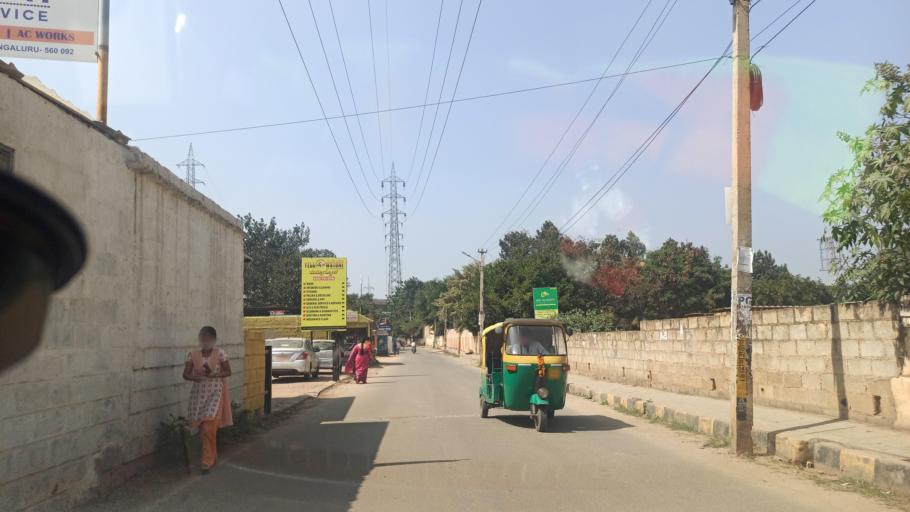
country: IN
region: Karnataka
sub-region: Bangalore Urban
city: Yelahanka
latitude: 13.0580
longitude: 77.5959
